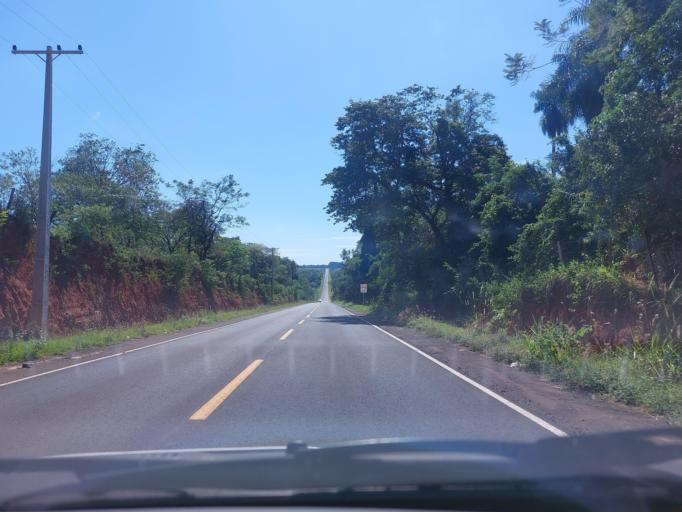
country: PY
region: San Pedro
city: Guayaybi
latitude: -24.5536
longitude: -56.5196
